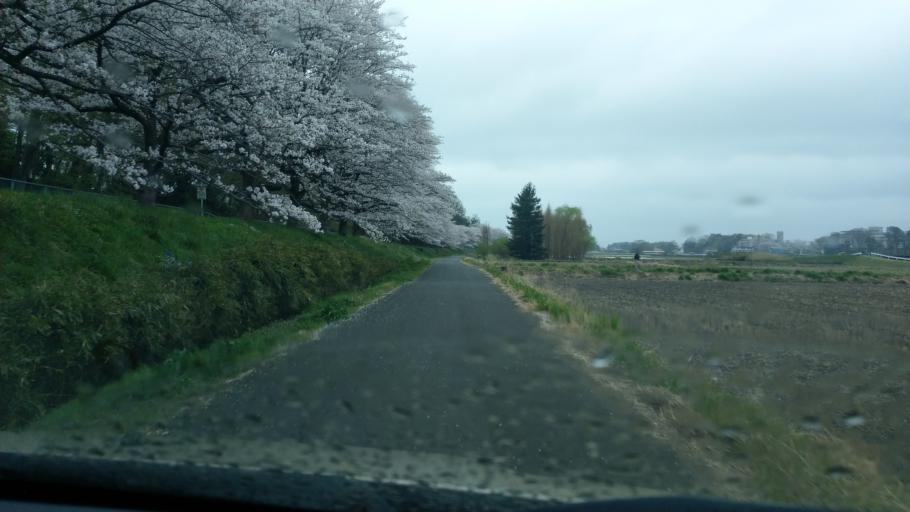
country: JP
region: Saitama
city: Saitama
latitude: 35.9128
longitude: 139.6919
